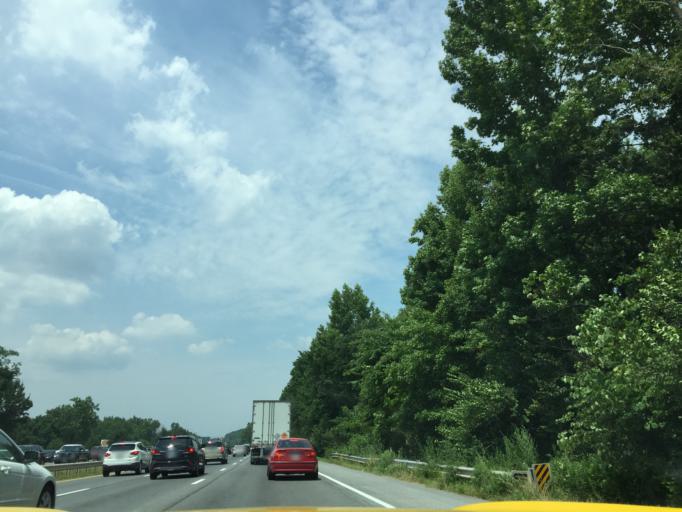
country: US
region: Maryland
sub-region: Prince George's County
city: Friendly
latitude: 38.7632
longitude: -76.9938
